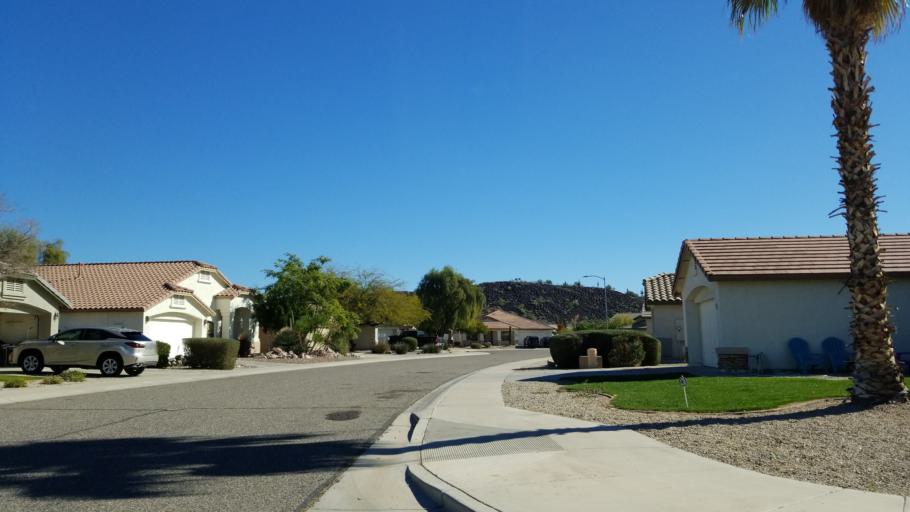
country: US
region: Arizona
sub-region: Maricopa County
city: Peoria
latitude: 33.6977
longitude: -112.1307
